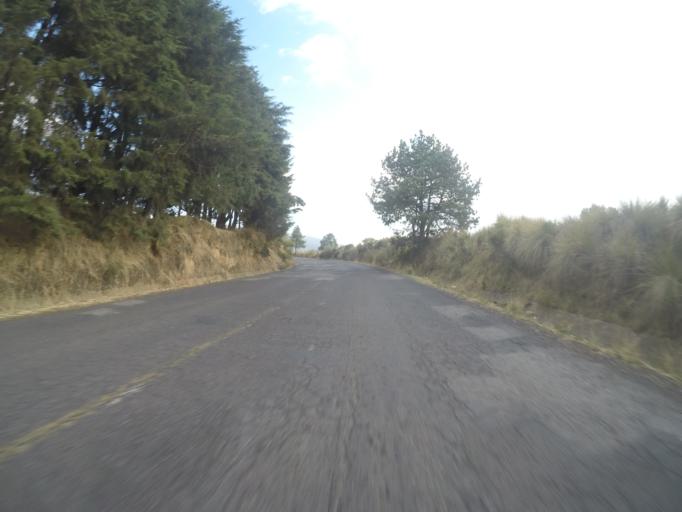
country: MX
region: Mexico
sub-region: Xalatlaco
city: San Juan Tomasquillo Herradura
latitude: 19.1630
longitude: -99.3905
